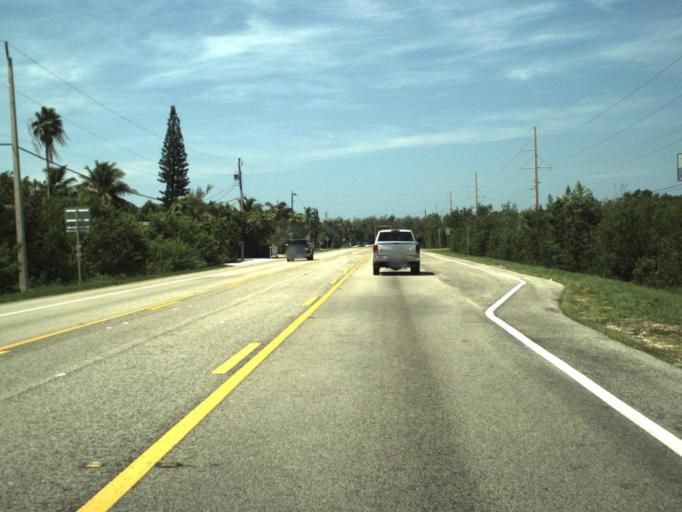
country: US
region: Florida
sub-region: Monroe County
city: Marathon
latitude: 24.7583
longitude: -80.9566
